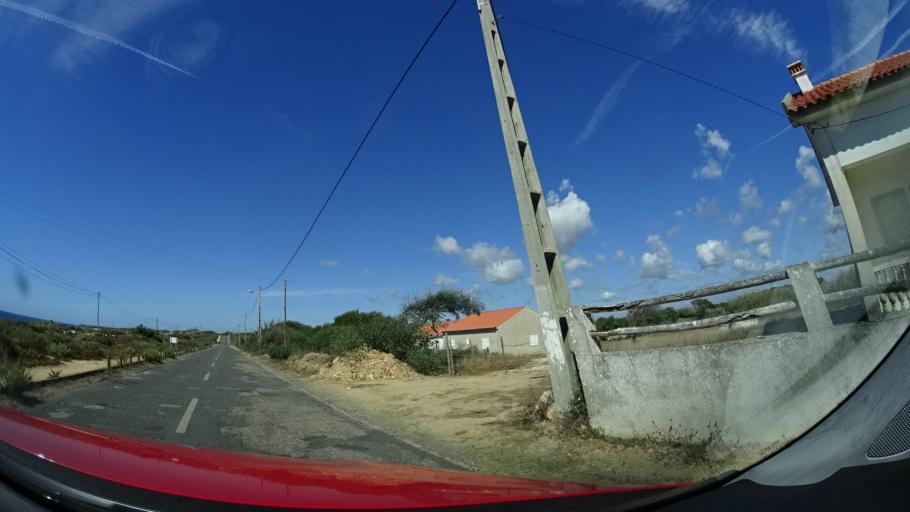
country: PT
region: Beja
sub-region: Odemira
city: Sao Teotonio
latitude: 37.5292
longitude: -8.7843
